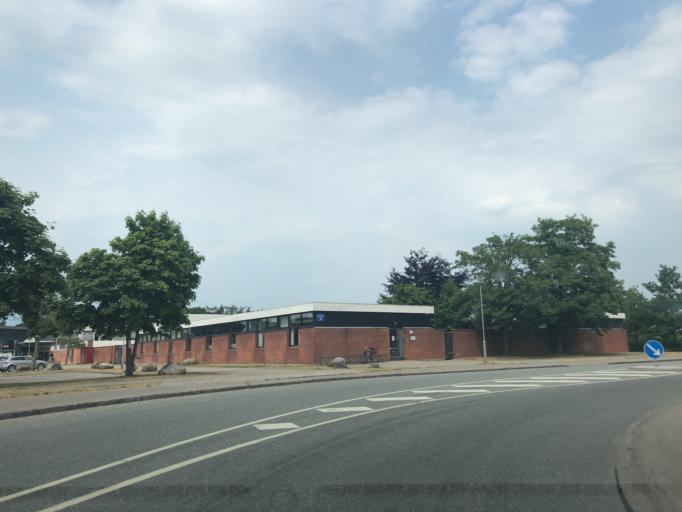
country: DK
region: Zealand
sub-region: Koge Kommune
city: Koge
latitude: 55.4528
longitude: 12.1681
